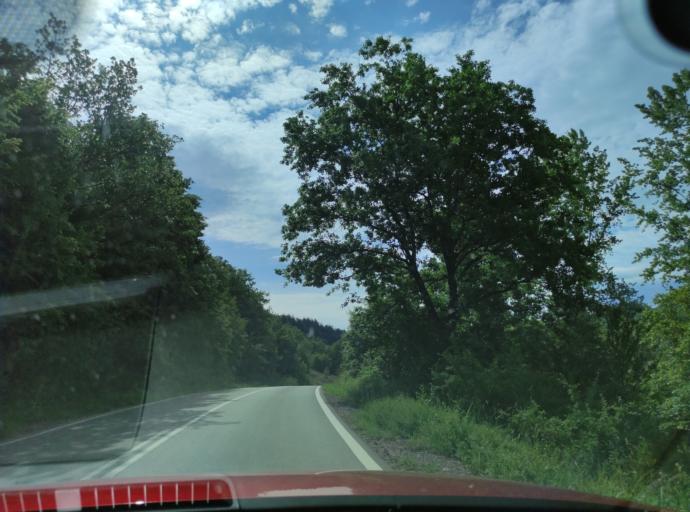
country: BG
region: Montana
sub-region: Obshtina Chiprovtsi
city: Chiprovtsi
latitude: 43.4558
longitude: 22.9018
